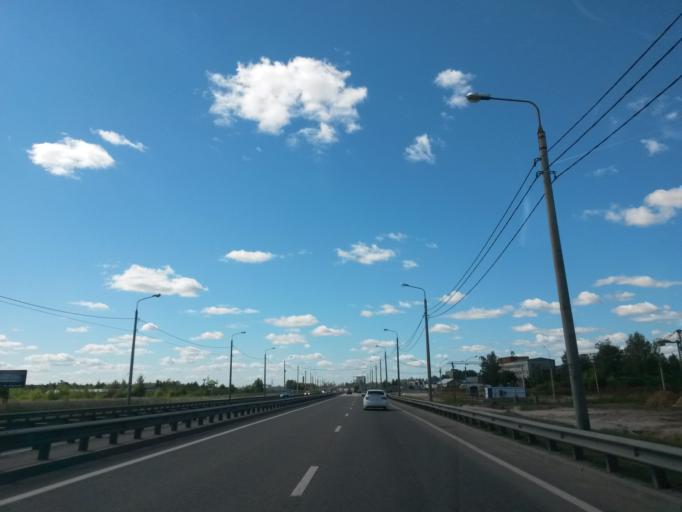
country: RU
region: Jaroslavl
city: Yaroslavl
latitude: 57.6695
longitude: 39.7946
